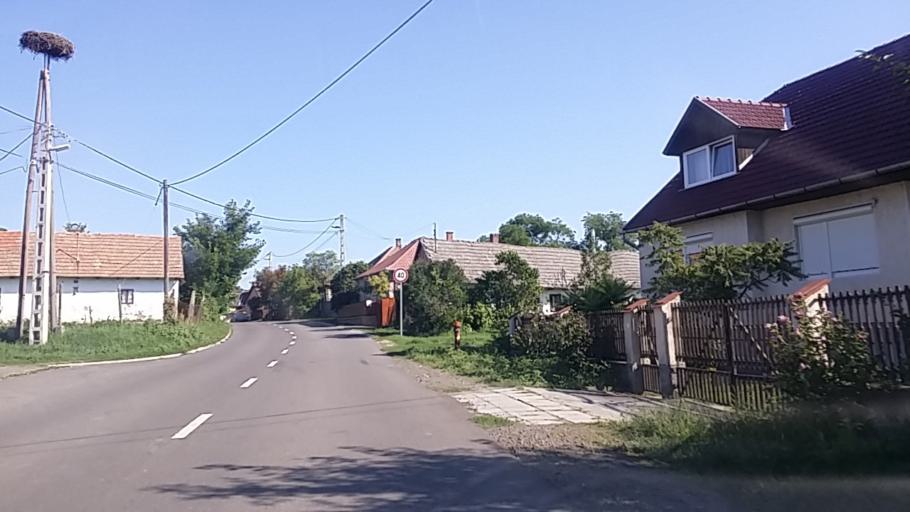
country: HU
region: Nograd
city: Jobbagyi
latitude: 47.8634
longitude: 19.6260
